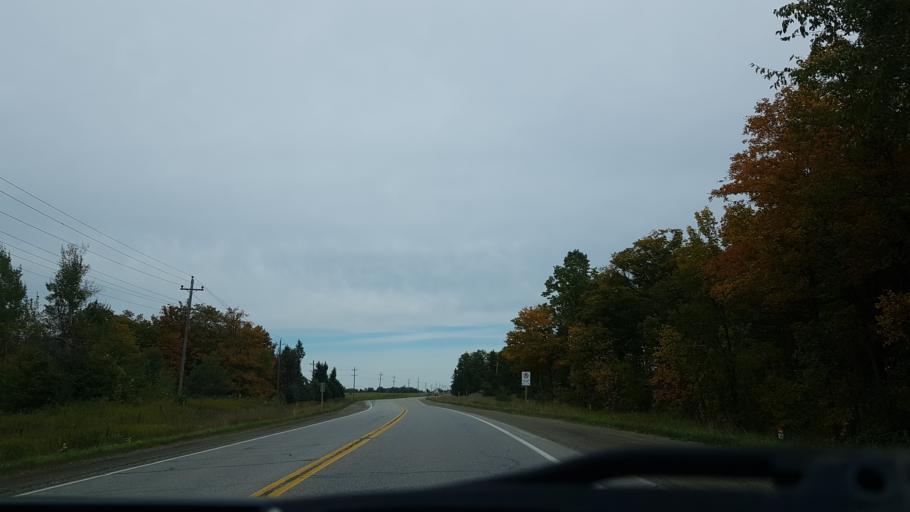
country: CA
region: Ontario
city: Orangeville
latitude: 43.8149
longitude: -80.0456
